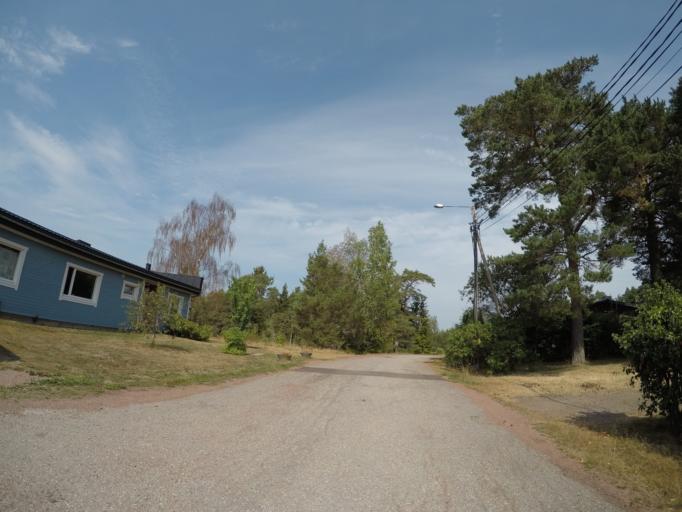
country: AX
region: Alands landsbygd
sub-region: Saltvik
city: Saltvik
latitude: 60.2324
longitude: 20.0011
